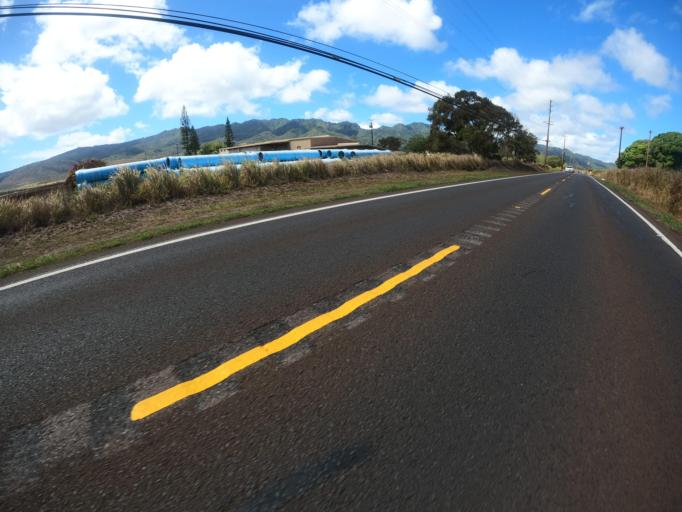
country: US
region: Hawaii
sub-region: Honolulu County
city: Village Park
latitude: 21.4188
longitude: -158.0487
